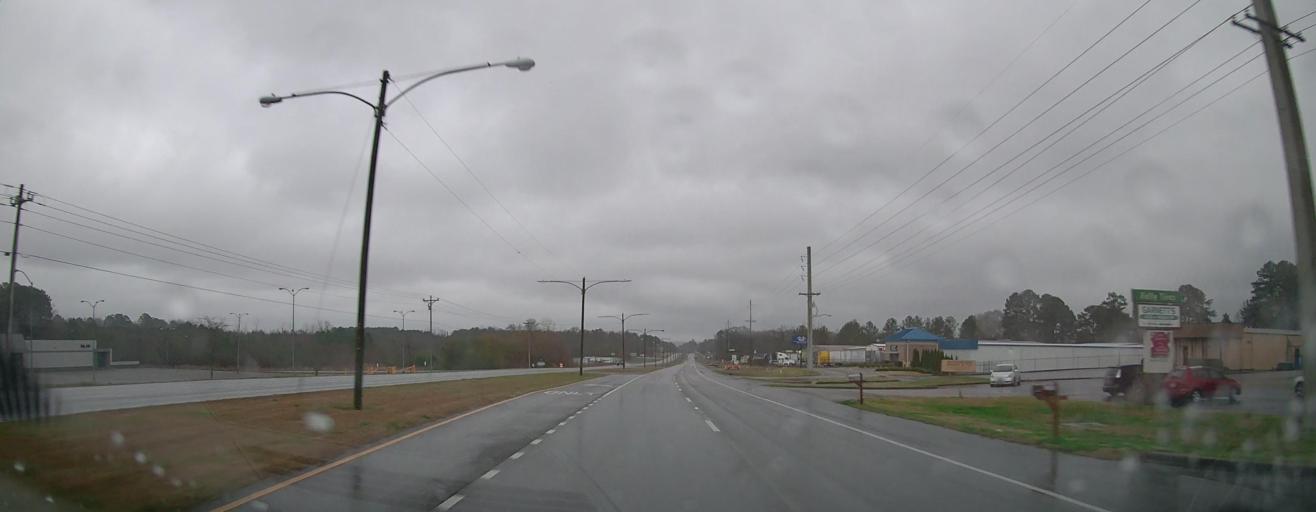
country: US
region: Alabama
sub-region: Morgan County
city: Hartselle
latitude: 34.4211
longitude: -86.9257
